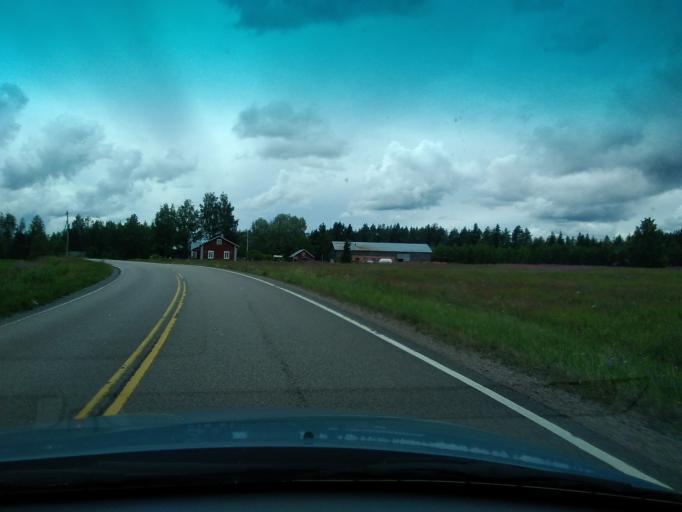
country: FI
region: Central Finland
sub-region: Saarijaervi-Viitasaari
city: Pylkoenmaeki
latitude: 62.6263
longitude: 24.7851
